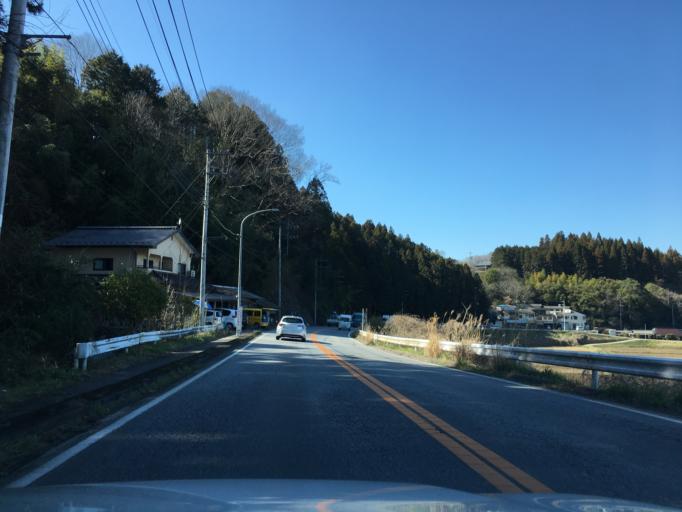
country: JP
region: Tochigi
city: Motegi
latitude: 36.5556
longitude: 140.2399
